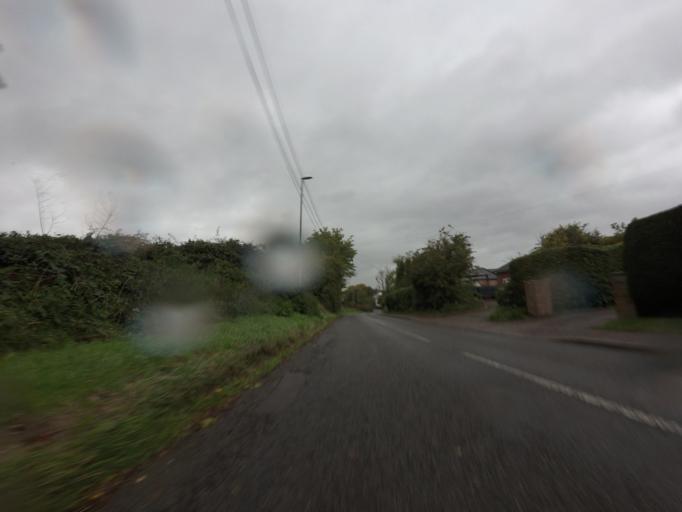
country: GB
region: England
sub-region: Cambridgeshire
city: Wimpole
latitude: 52.1885
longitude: -0.0612
